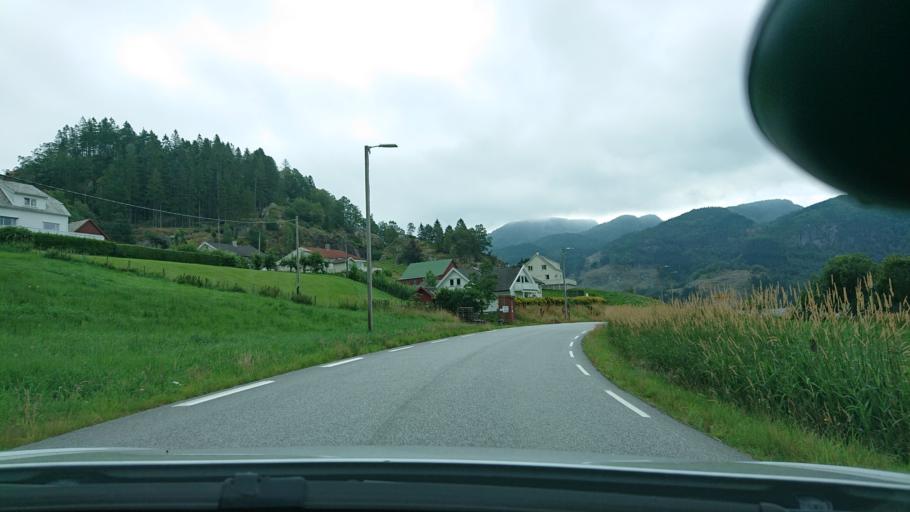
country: NO
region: Rogaland
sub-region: Hjelmeland
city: Hjelmelandsvagen
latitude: 59.2336
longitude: 6.1892
